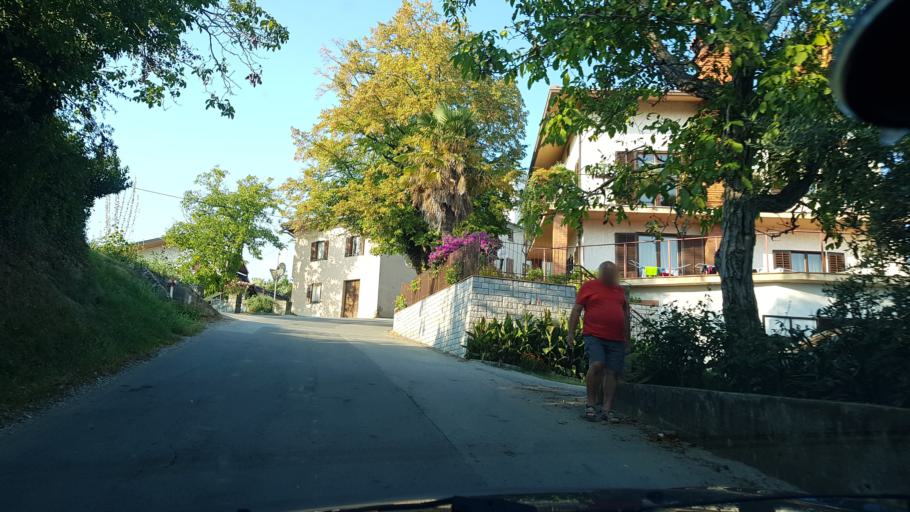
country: IT
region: Friuli Venezia Giulia
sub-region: Provincia di Gorizia
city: San Floriano del Collio
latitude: 45.9813
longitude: 13.5628
